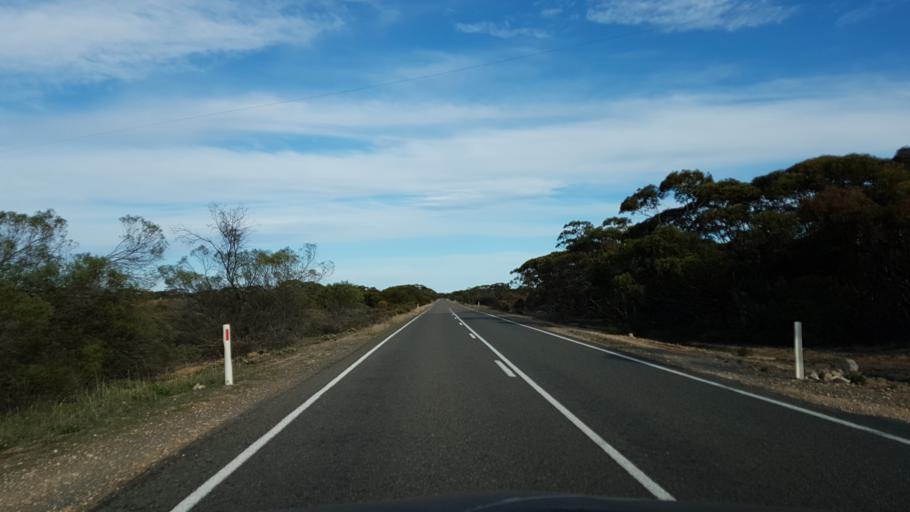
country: AU
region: South Australia
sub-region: Mid Murray
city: Mannum
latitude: -35.0101
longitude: 139.5212
